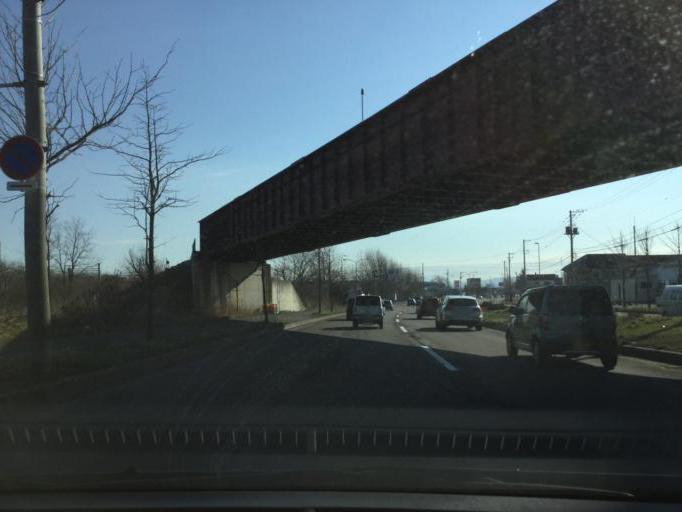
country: JP
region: Hokkaido
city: Iwamizawa
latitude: 43.1864
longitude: 141.7251
